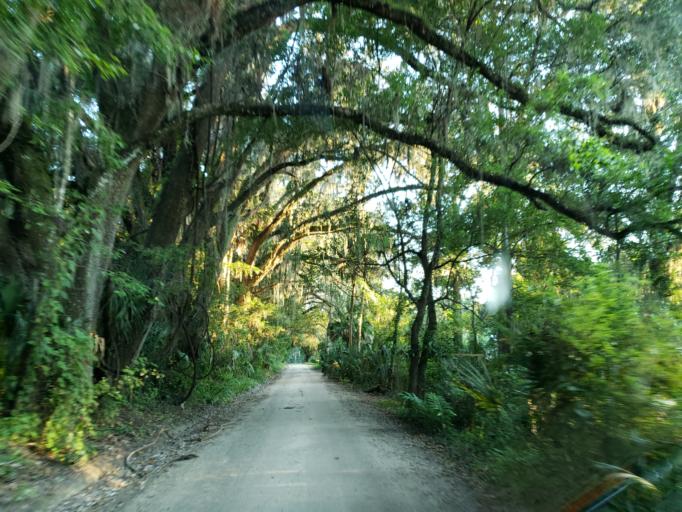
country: US
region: Florida
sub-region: Alachua County
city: Gainesville
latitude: 29.4984
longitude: -82.2827
